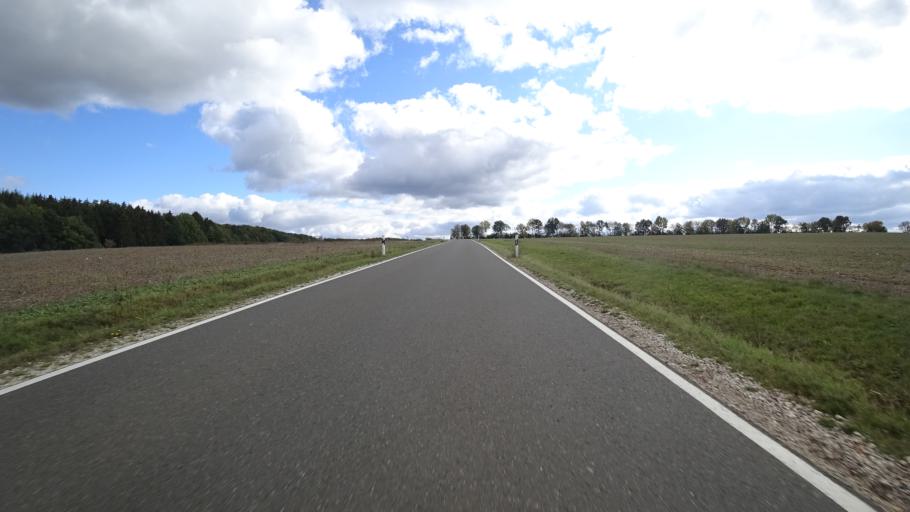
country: DE
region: Rheinland-Pfalz
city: Morschbach
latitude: 50.0208
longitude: 7.6169
